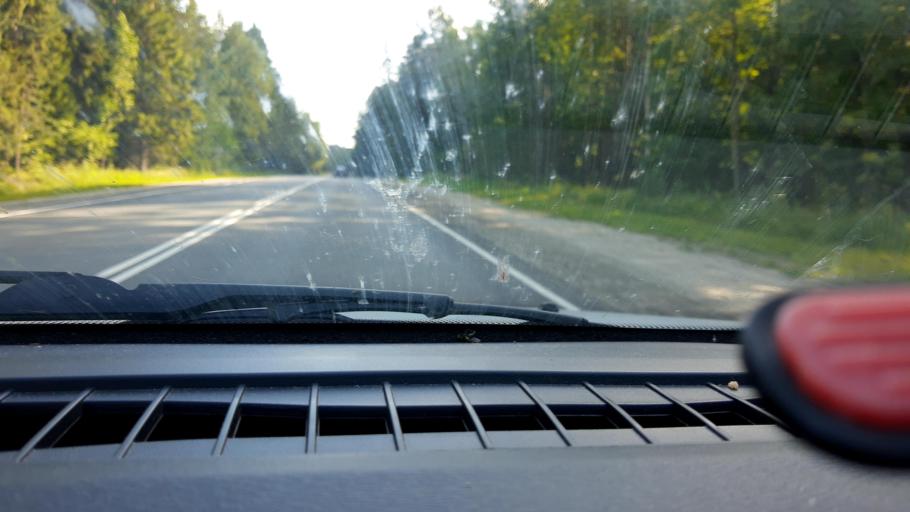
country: RU
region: Nizjnij Novgorod
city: Semenov
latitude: 56.7510
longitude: 44.3598
